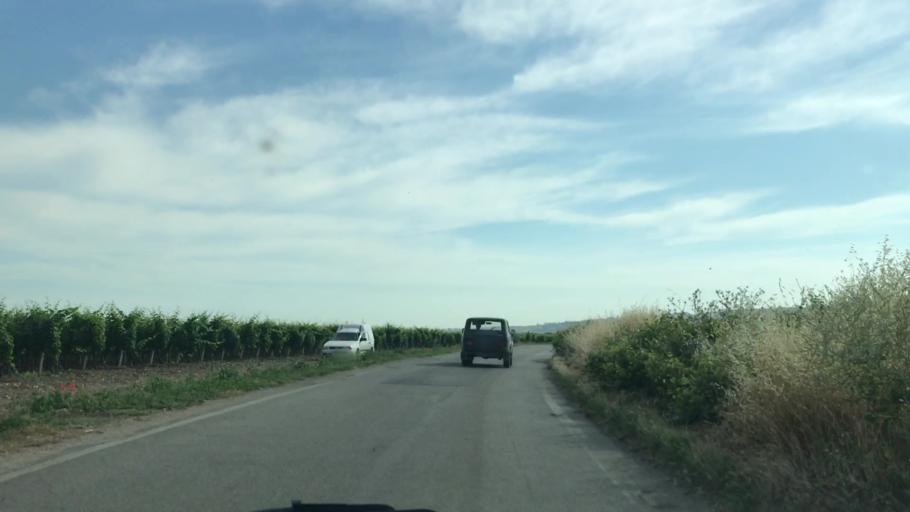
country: IT
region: Apulia
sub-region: Provincia di Taranto
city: San Giorgio Ionico
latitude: 40.4351
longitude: 17.3469
